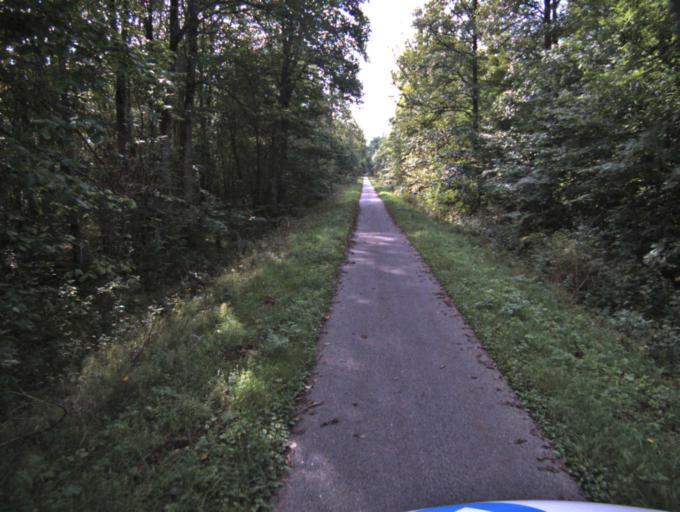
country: SE
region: Vaestra Goetaland
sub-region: Tranemo Kommun
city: Limmared
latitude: 57.6518
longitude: 13.3612
